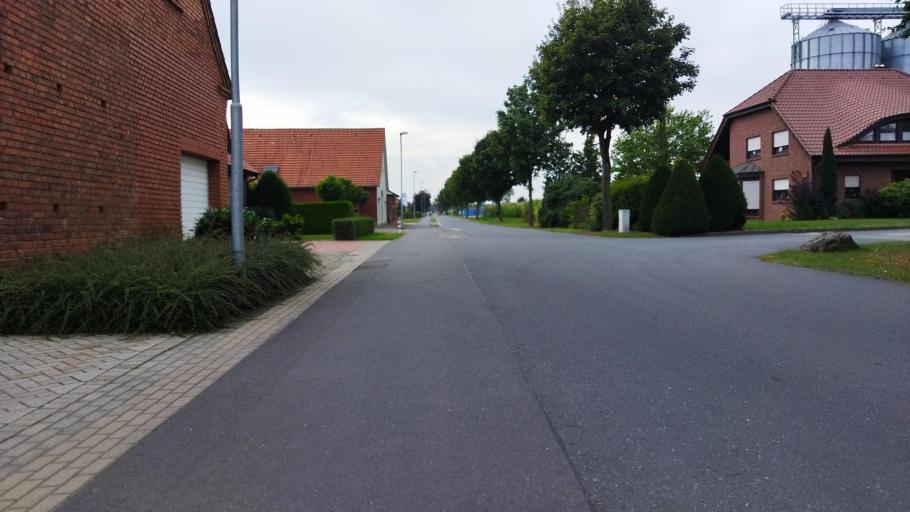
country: DE
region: Lower Saxony
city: Bad Laer
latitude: 52.1015
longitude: 8.0669
